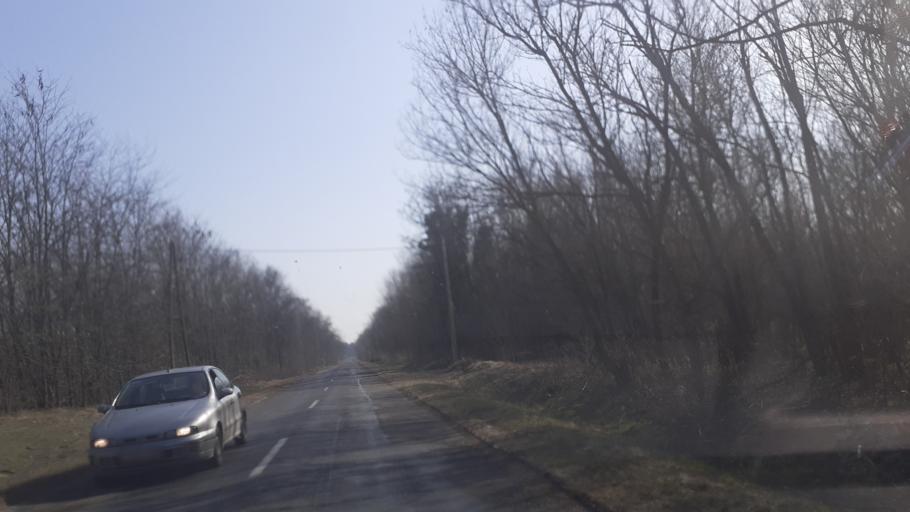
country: HU
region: Pest
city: Orkeny
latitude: 47.0650
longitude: 19.3958
